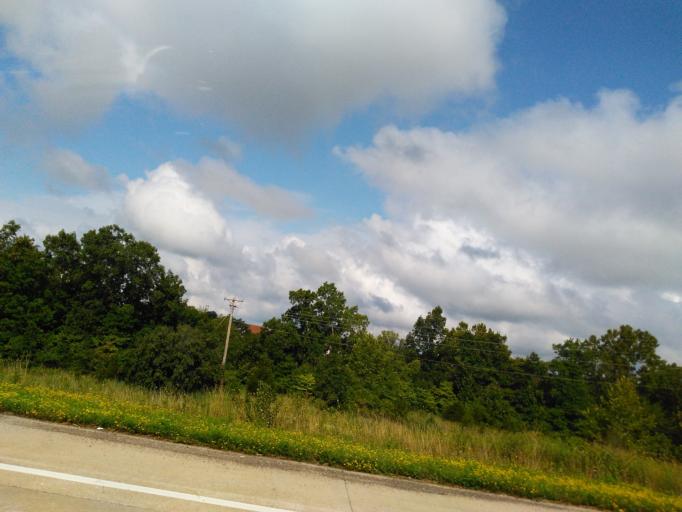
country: US
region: Missouri
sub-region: Jefferson County
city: Hillsboro
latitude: 38.2611
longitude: -90.5540
